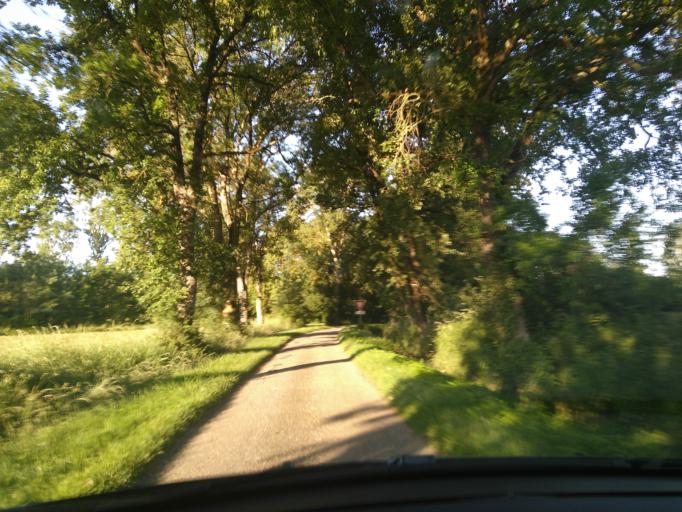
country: FR
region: Midi-Pyrenees
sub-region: Departement du Gers
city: Valence-sur-Baise
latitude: 43.8686
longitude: 0.4508
